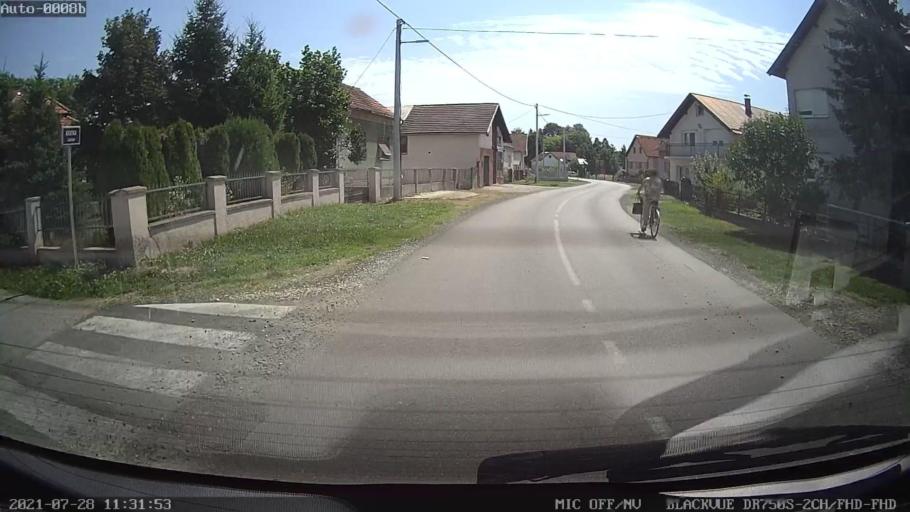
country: HR
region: Medimurska
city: Kursanec
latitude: 46.2824
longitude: 16.3981
